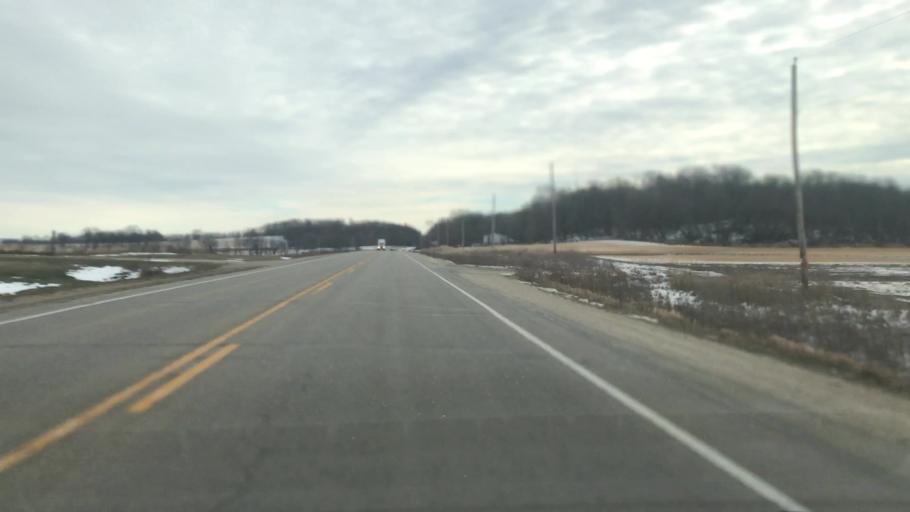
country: US
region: Wisconsin
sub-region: Dodge County
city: Mayville
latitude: 43.4418
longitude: -88.4887
